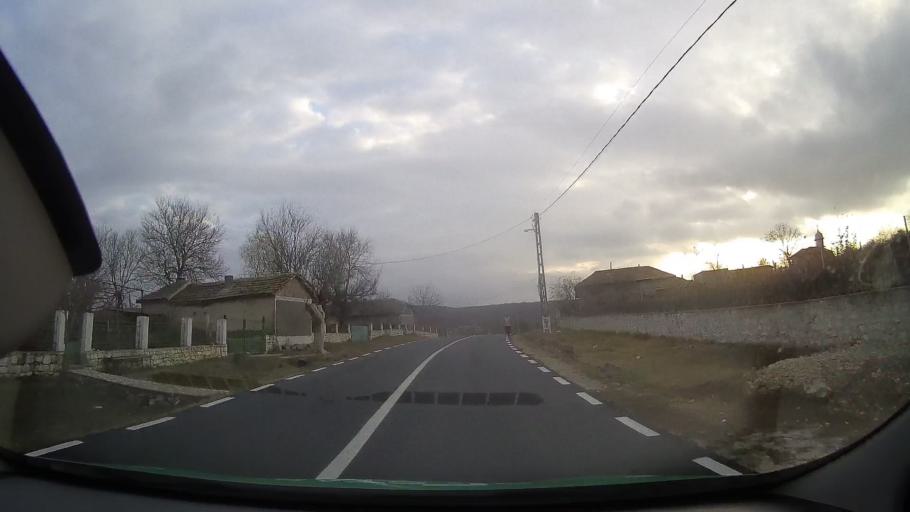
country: RO
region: Constanta
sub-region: Comuna Adamclisi
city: Adamclisi
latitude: 44.0474
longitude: 27.9613
